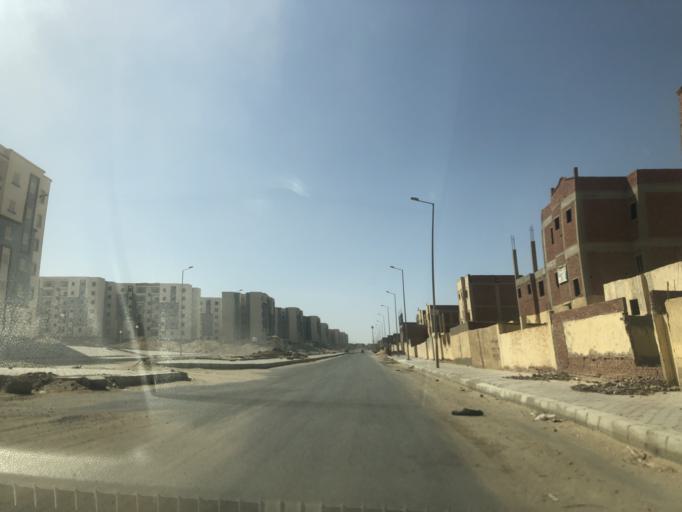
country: EG
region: Al Jizah
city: Madinat Sittah Uktubar
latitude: 29.9312
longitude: 30.9870
